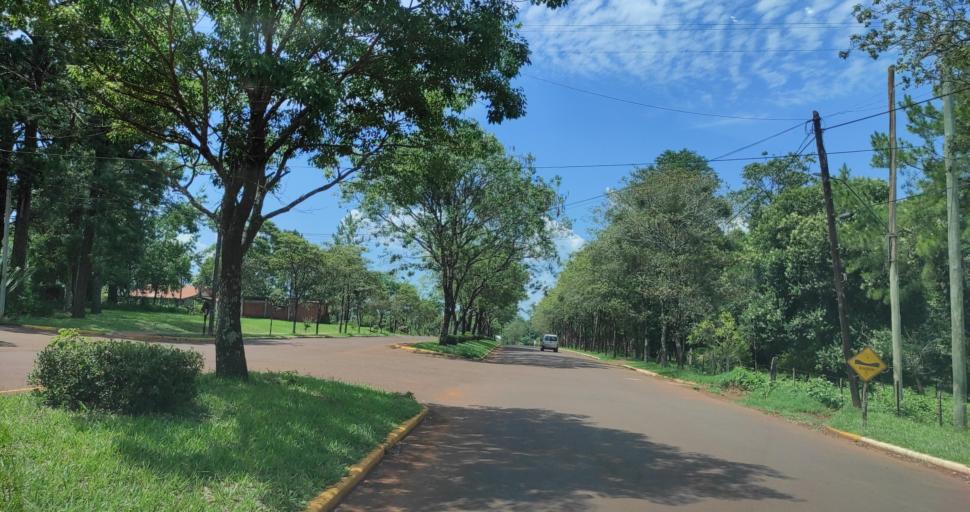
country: AR
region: Misiones
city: Ruiz de Montoya
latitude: -26.9743
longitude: -55.0517
